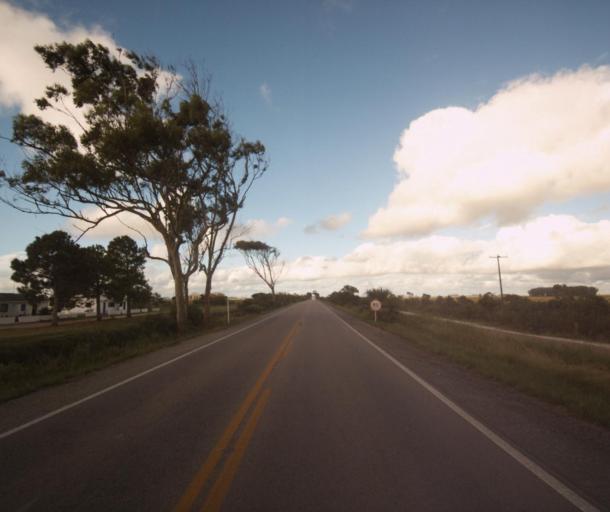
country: BR
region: Rio Grande do Sul
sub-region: Rio Grande
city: Rio Grande
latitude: -32.1942
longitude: -52.4374
